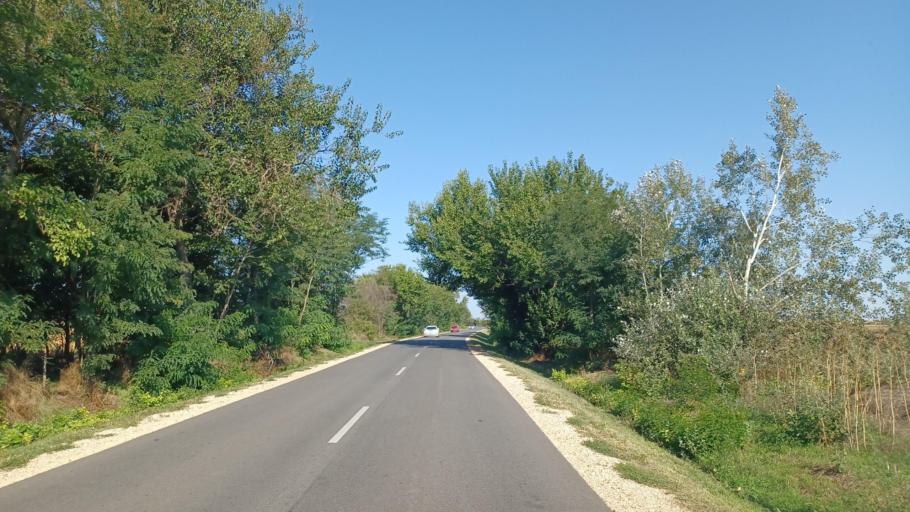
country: HU
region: Tolna
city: Nemetker
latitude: 46.6936
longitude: 18.7964
